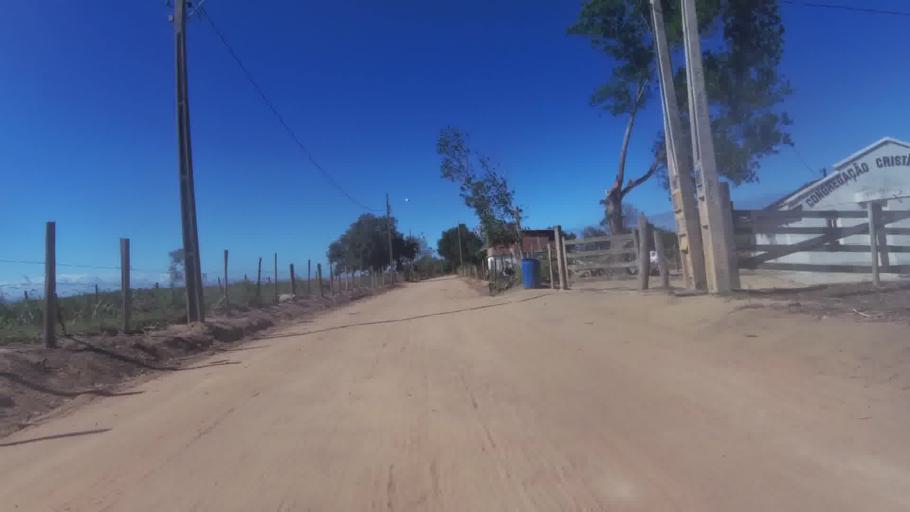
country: BR
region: Espirito Santo
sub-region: Marataizes
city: Marataizes
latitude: -21.1355
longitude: -40.9917
